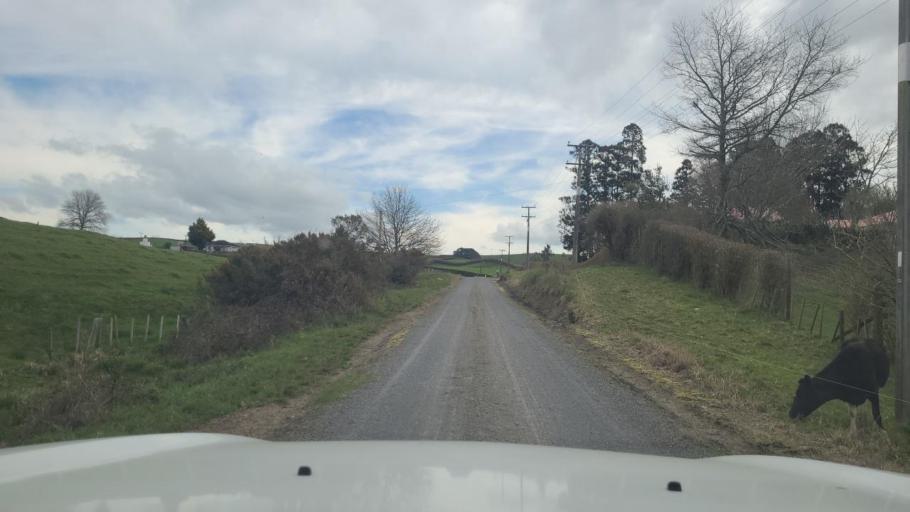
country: NZ
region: Waikato
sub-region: Matamata-Piako District
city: Matamata
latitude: -37.7586
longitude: 175.6208
